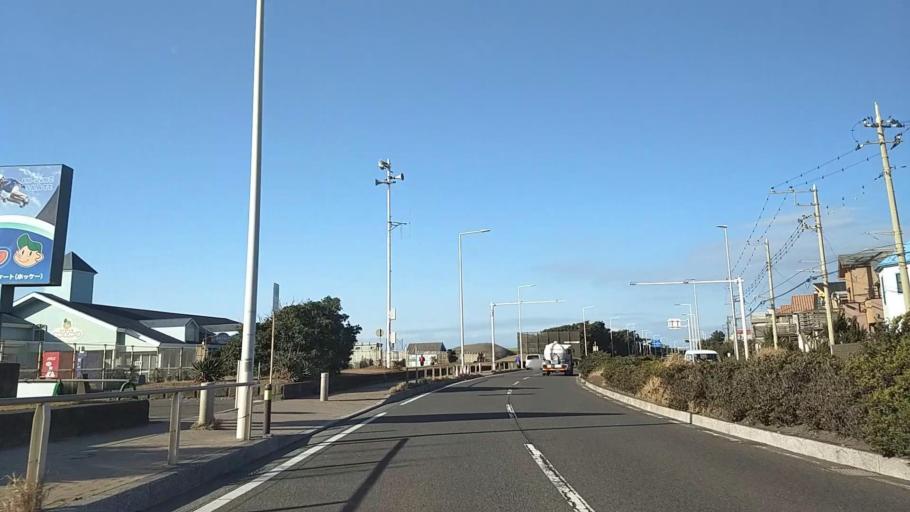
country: JP
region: Kanagawa
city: Fujisawa
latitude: 35.3169
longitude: 139.4665
